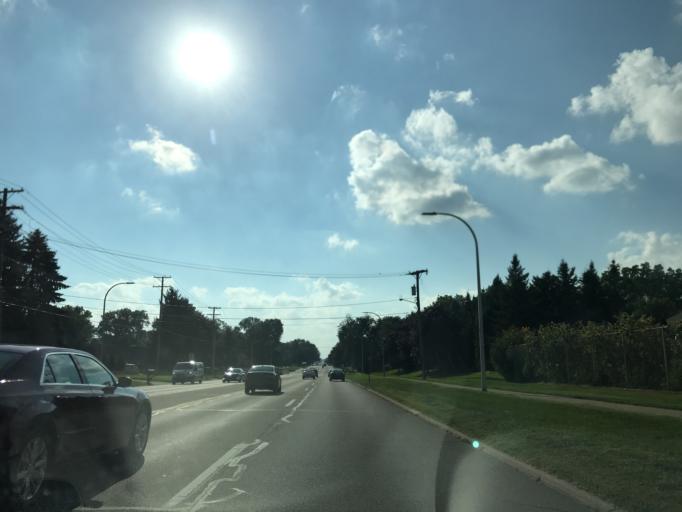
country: US
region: Michigan
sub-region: Wayne County
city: Livonia
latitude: 42.3970
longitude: -83.3874
